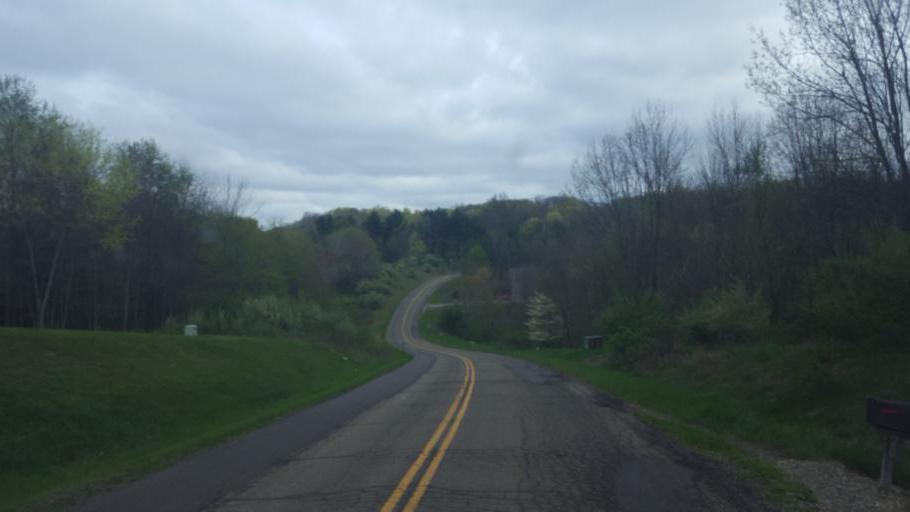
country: US
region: Ohio
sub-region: Knox County
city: Gambier
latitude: 40.4397
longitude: -82.3536
